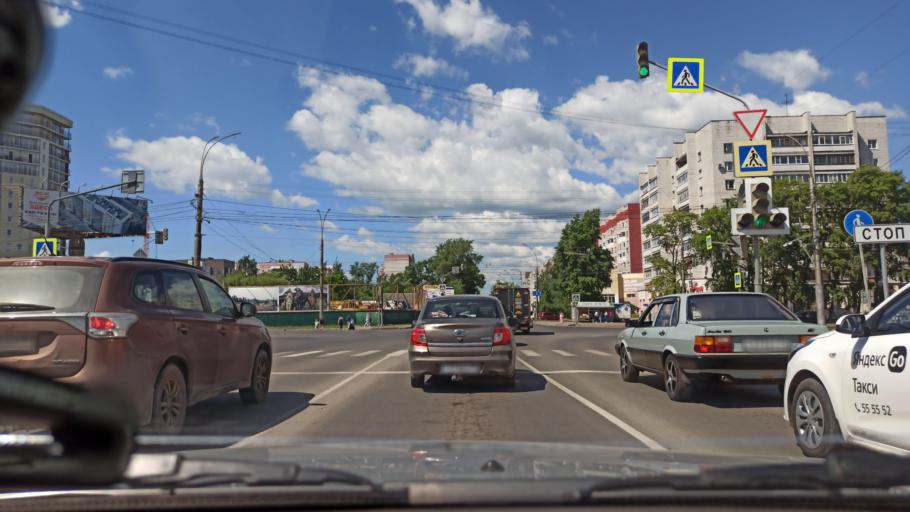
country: RU
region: Vologda
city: Vologda
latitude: 59.2118
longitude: 39.8530
